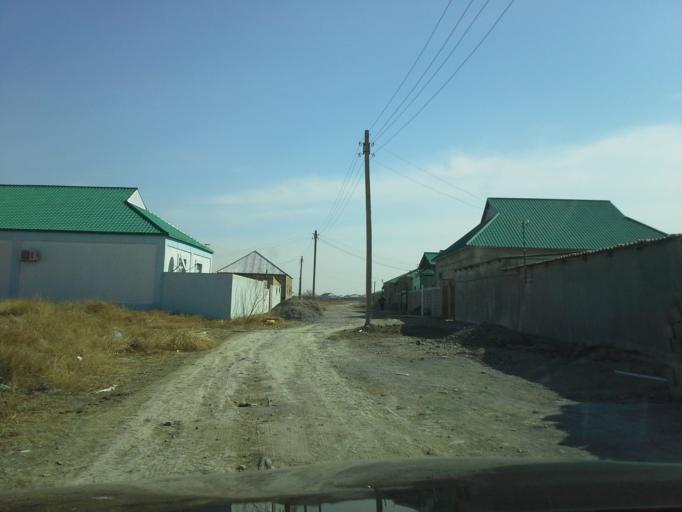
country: TM
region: Ahal
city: Abadan
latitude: 38.1031
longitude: 58.0319
